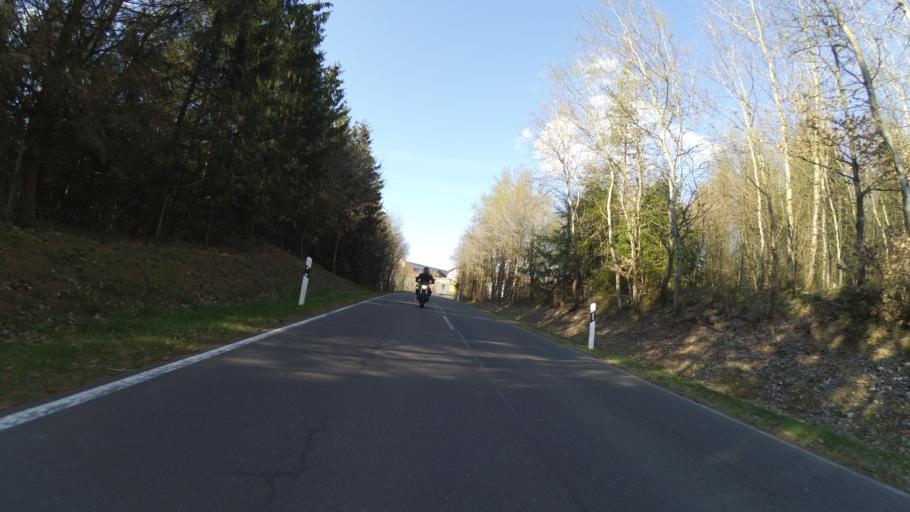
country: DE
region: Rheinland-Pfalz
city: Nurburg
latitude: 50.3282
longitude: 6.9452
